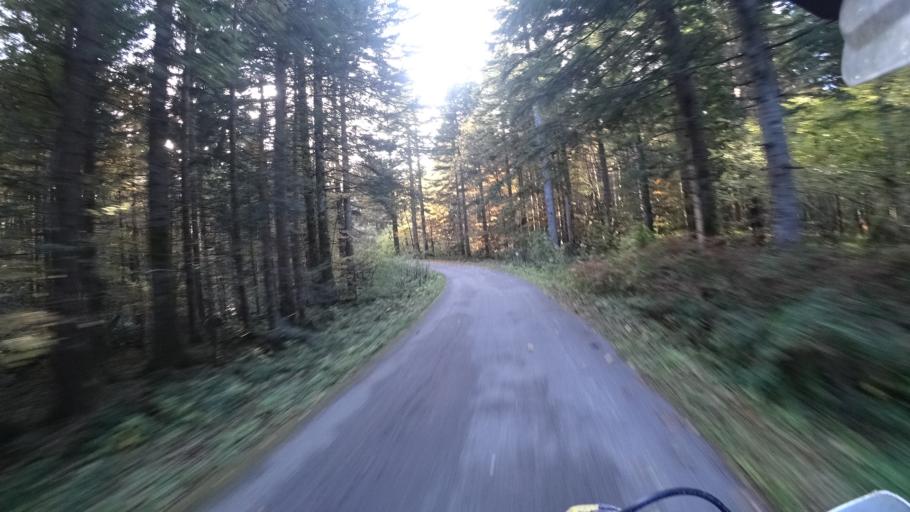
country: HR
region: Karlovacka
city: Plaski
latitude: 44.9829
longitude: 15.4047
